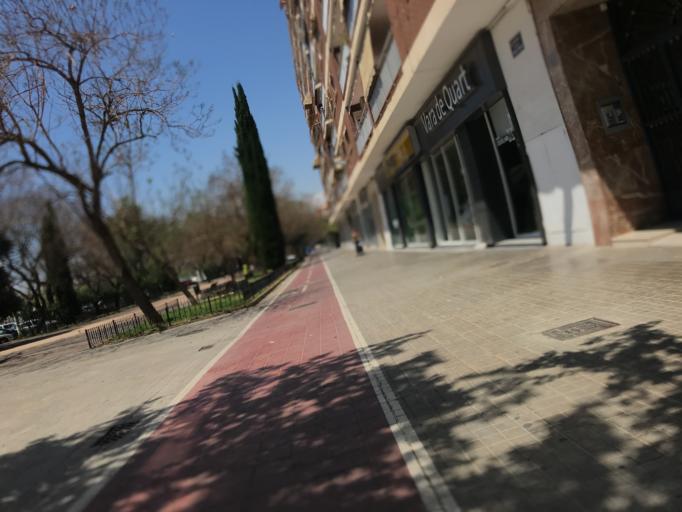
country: ES
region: Valencia
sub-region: Provincia de Valencia
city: Mislata
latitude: 39.4586
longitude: -0.4022
